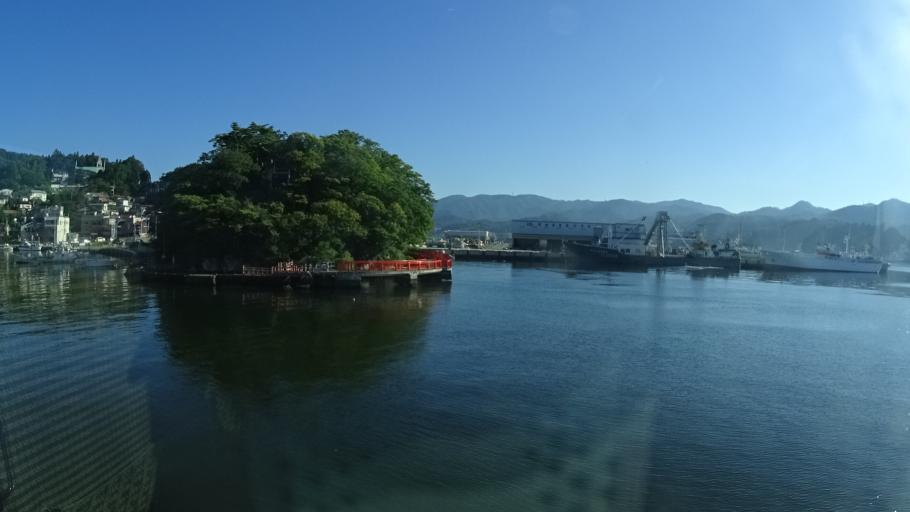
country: JP
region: Iwate
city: Ofunato
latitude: 38.9057
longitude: 141.5791
